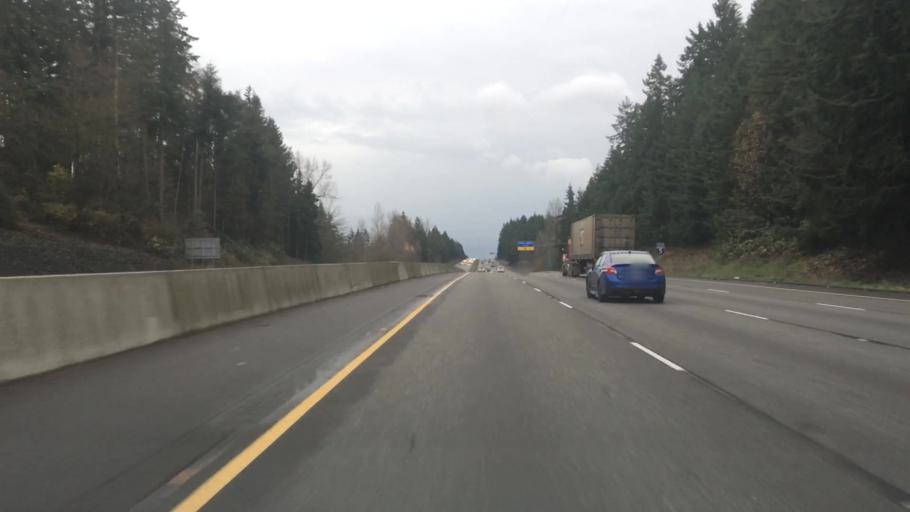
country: US
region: Washington
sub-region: Thurston County
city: Grand Mound
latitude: 46.8907
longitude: -122.9628
